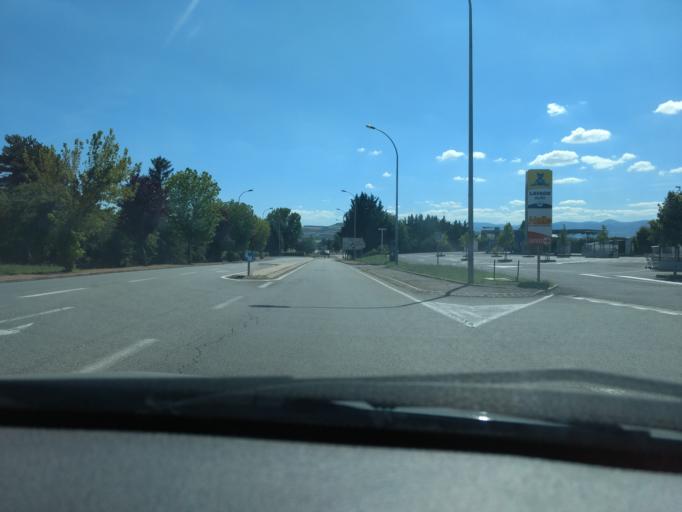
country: FR
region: Auvergne
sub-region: Departement du Puy-de-Dome
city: Pont-du-Chateau
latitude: 45.7942
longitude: 3.2294
